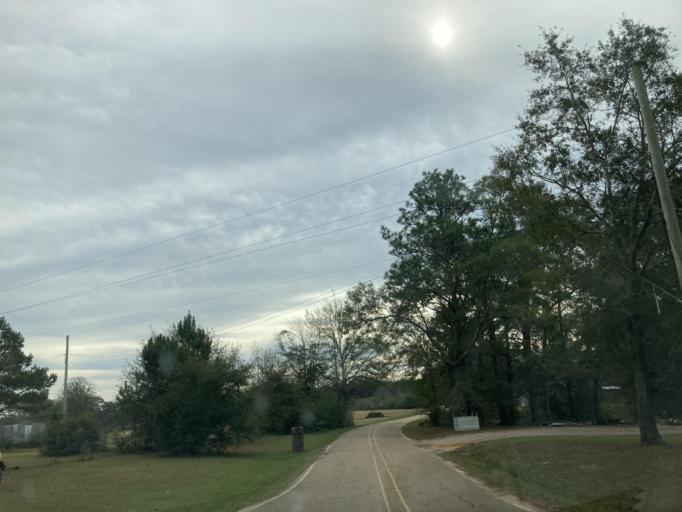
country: US
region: Mississippi
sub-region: Lamar County
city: Purvis
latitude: 31.0964
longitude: -89.4679
